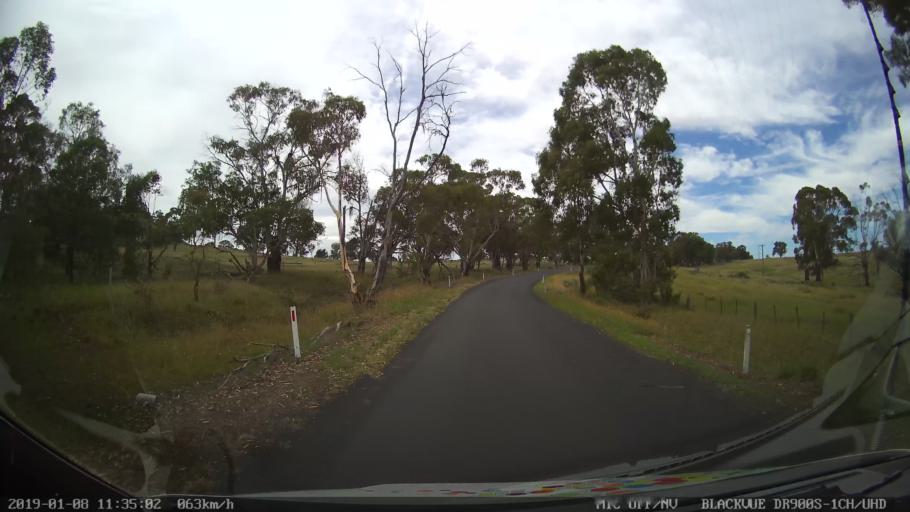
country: AU
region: New South Wales
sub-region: Guyra
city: Guyra
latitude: -30.3335
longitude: 151.5369
